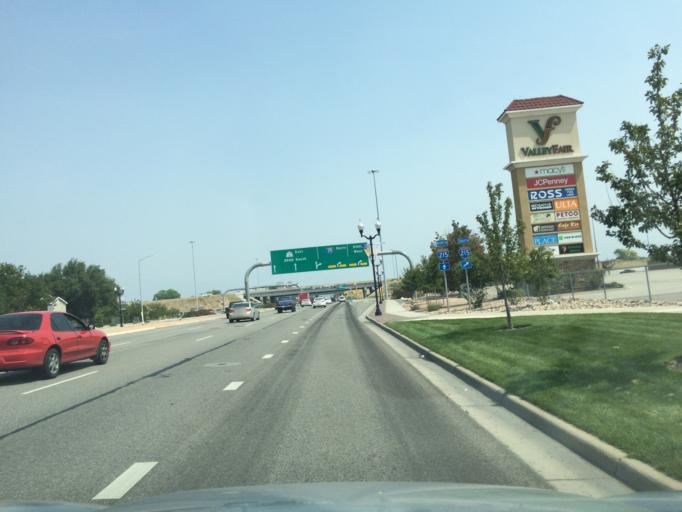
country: US
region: Utah
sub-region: Salt Lake County
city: Taylorsville
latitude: 40.6966
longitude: -111.9563
